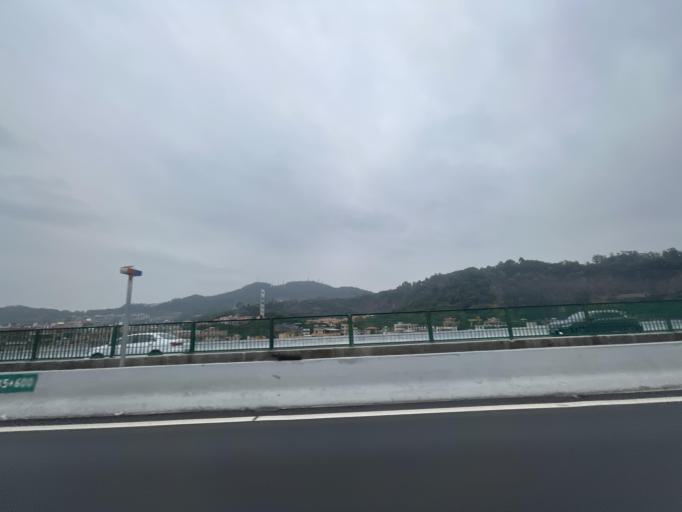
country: CN
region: Guangdong
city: Nansha
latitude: 22.7679
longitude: 113.5549
